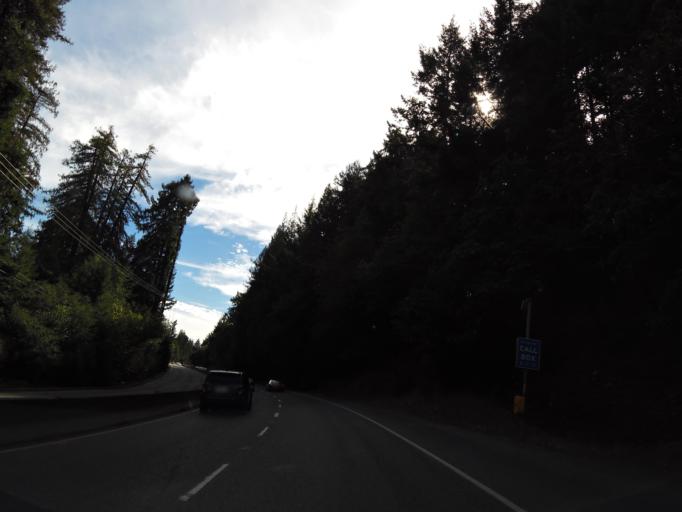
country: US
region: California
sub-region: Santa Clara County
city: Lexington Hills
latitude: 37.1755
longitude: -121.9962
